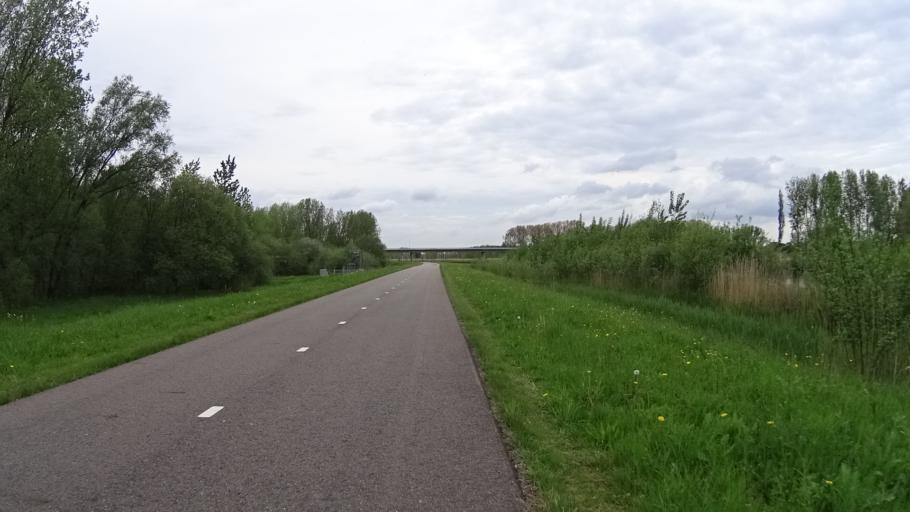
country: NL
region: North Brabant
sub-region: Gemeente Schijndel
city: Schijndel
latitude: 51.6408
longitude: 5.4701
